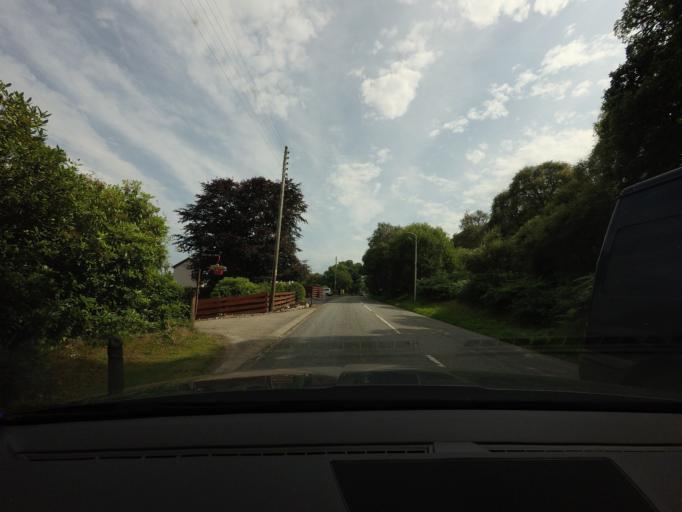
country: GB
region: Scotland
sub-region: Highland
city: Alness
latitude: 57.8789
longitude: -4.3604
